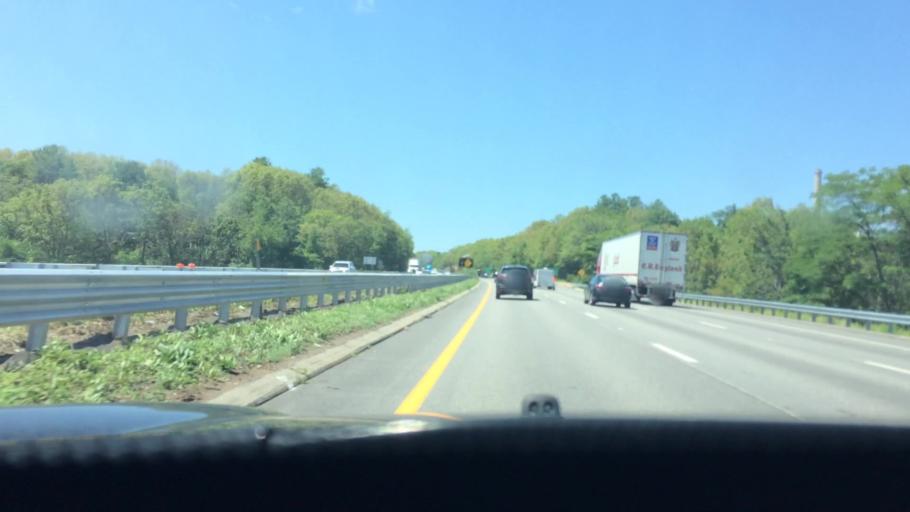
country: US
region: Massachusetts
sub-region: Worcester County
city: Millbury
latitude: 42.2209
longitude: -71.7572
